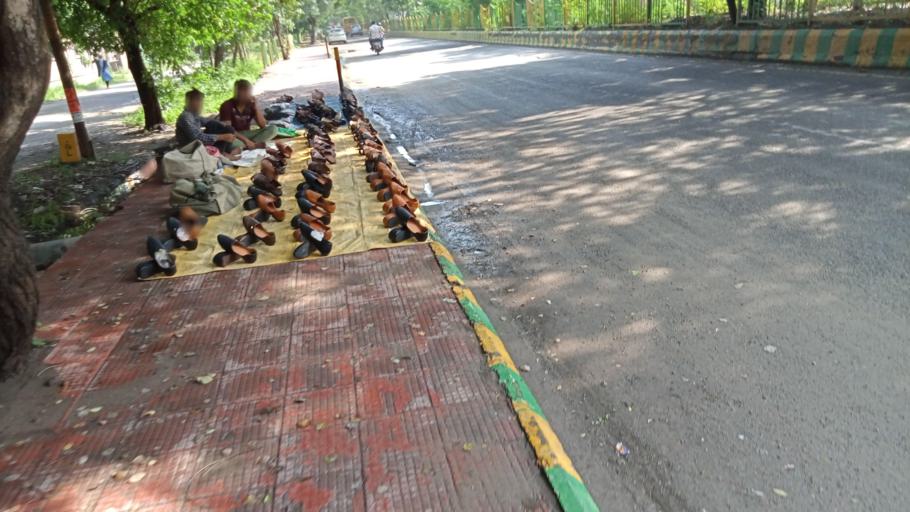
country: IN
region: Uttar Pradesh
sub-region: Ghaziabad
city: Ghaziabad
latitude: 28.6659
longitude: 77.3714
